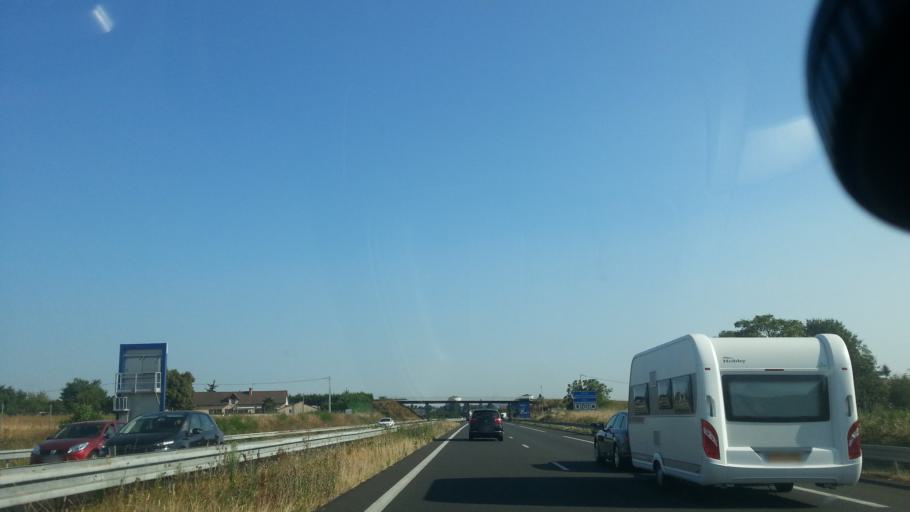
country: FR
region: Poitou-Charentes
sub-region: Departement de la Vienne
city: Chatellerault
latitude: 46.8111
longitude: 0.5140
